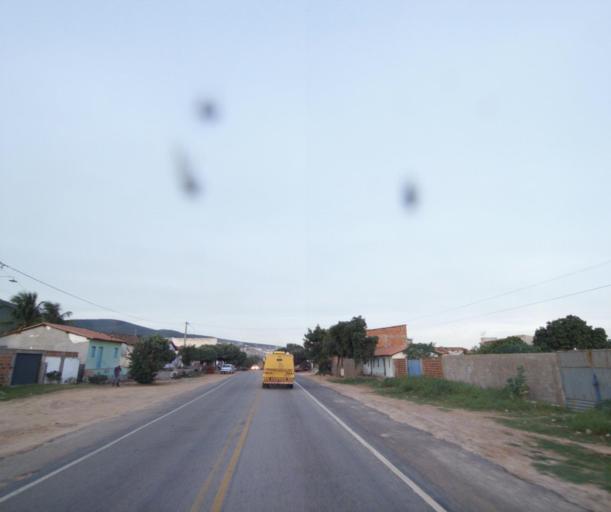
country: BR
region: Bahia
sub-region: Brumado
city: Brumado
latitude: -14.2513
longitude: -41.7349
